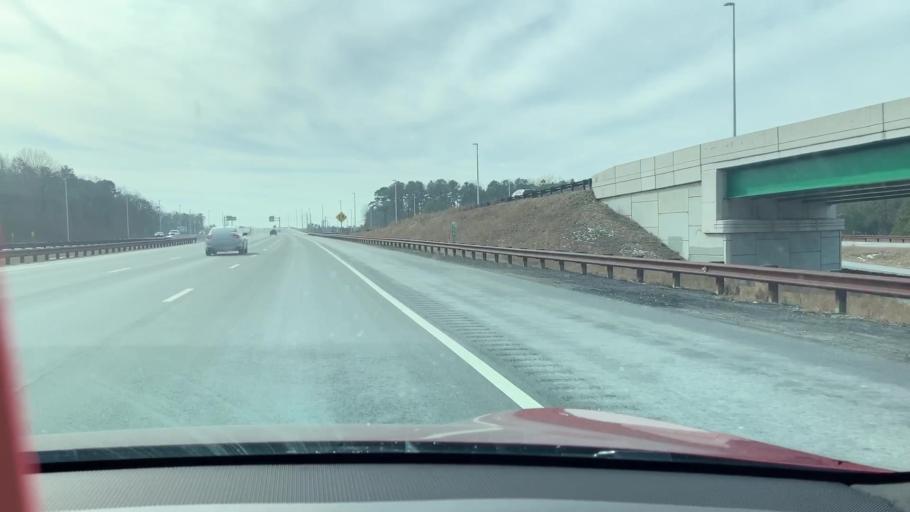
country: US
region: New Jersey
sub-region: Atlantic County
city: Pleasantville
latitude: 39.4099
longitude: -74.5556
